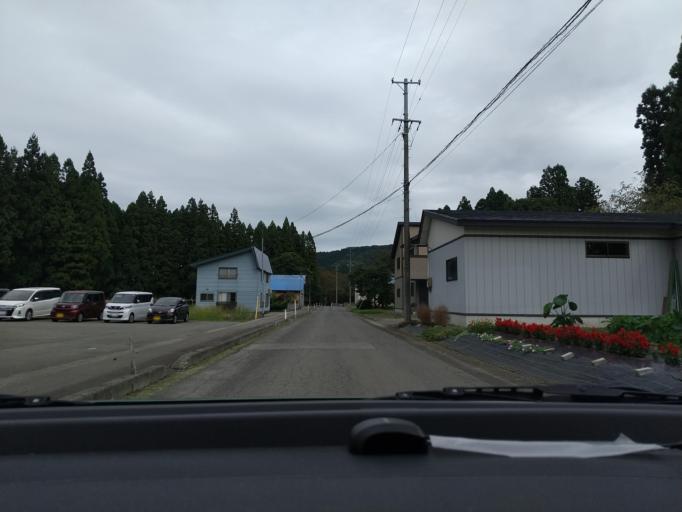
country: JP
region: Akita
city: Kakunodatemachi
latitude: 39.5900
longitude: 140.6107
